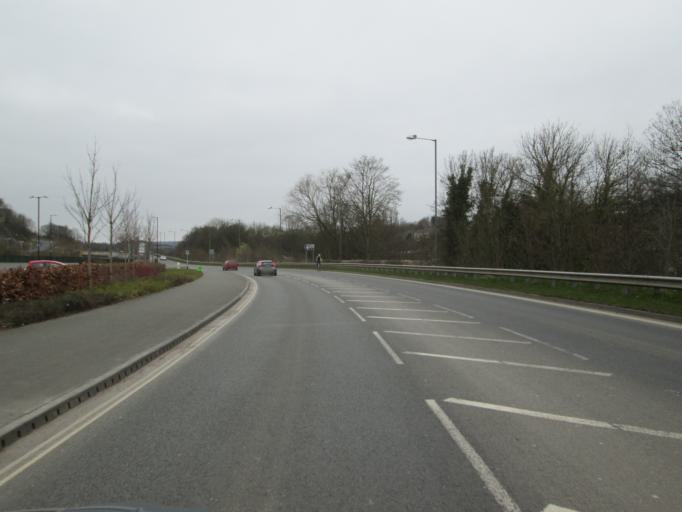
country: GB
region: England
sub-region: Derbyshire
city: Matlock
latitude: 53.1387
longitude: -1.5577
